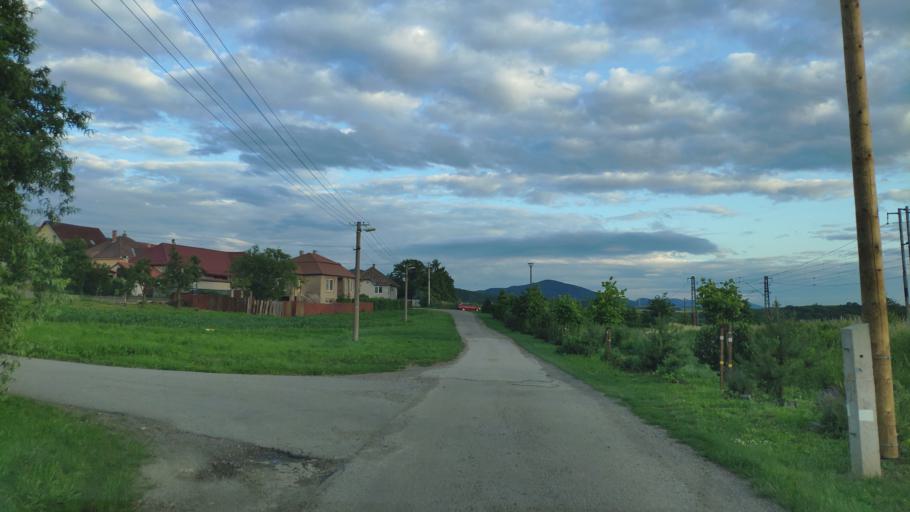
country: SK
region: Kosicky
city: Kosice
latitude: 48.6350
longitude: 21.3821
